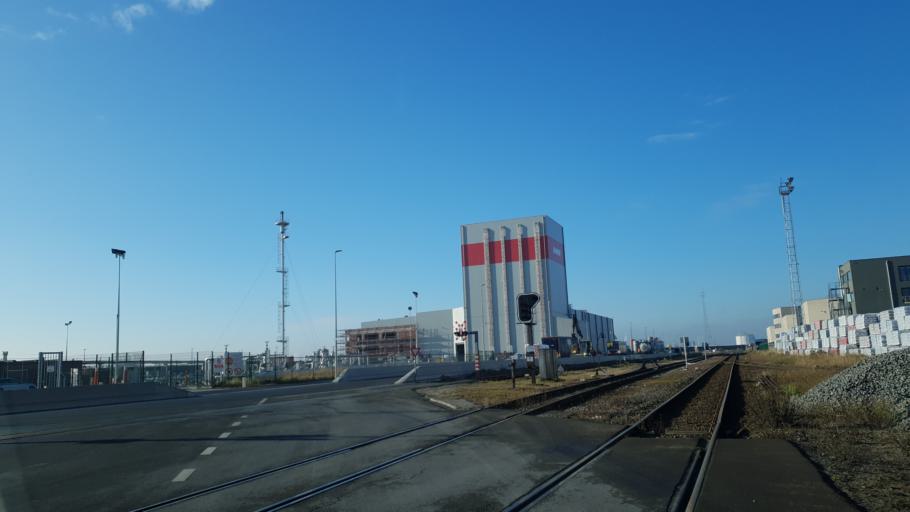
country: BE
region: Flanders
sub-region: Provincie Antwerpen
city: Zwijndrecht
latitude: 51.2442
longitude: 4.3601
